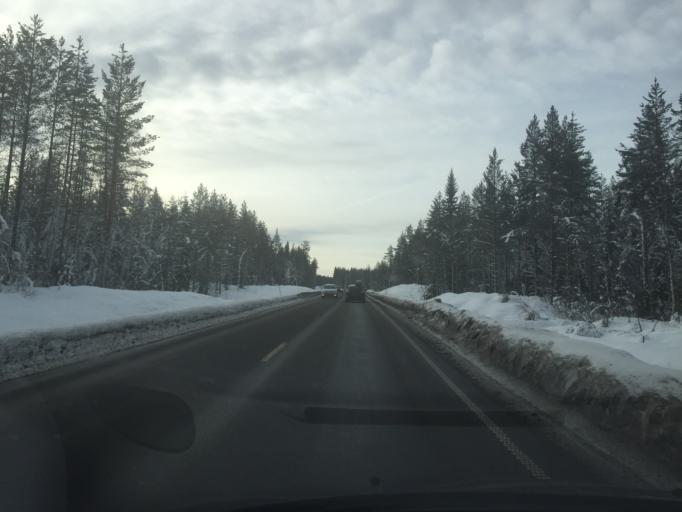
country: NO
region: Hedmark
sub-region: Trysil
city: Innbygda
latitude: 61.2563
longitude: 12.3025
